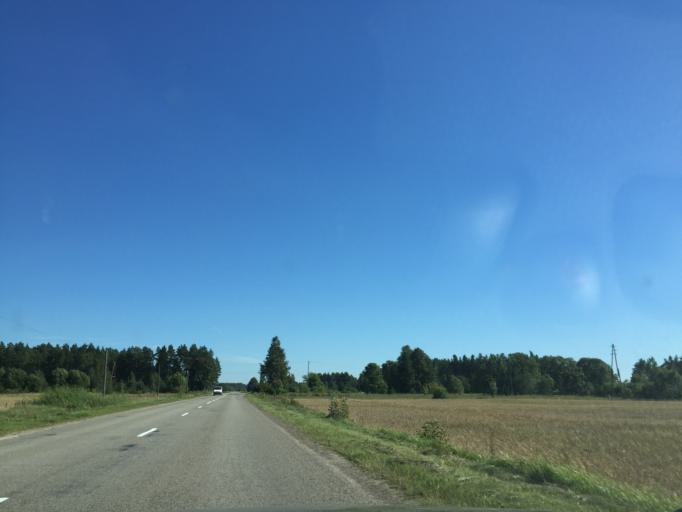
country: LV
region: Akniste
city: Akniste
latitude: 56.1475
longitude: 25.7890
